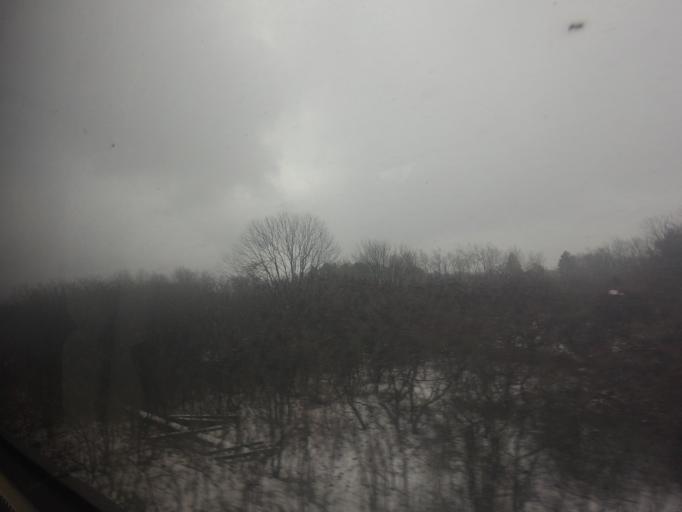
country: CA
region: Ontario
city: Cobourg
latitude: 43.9272
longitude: -78.4184
